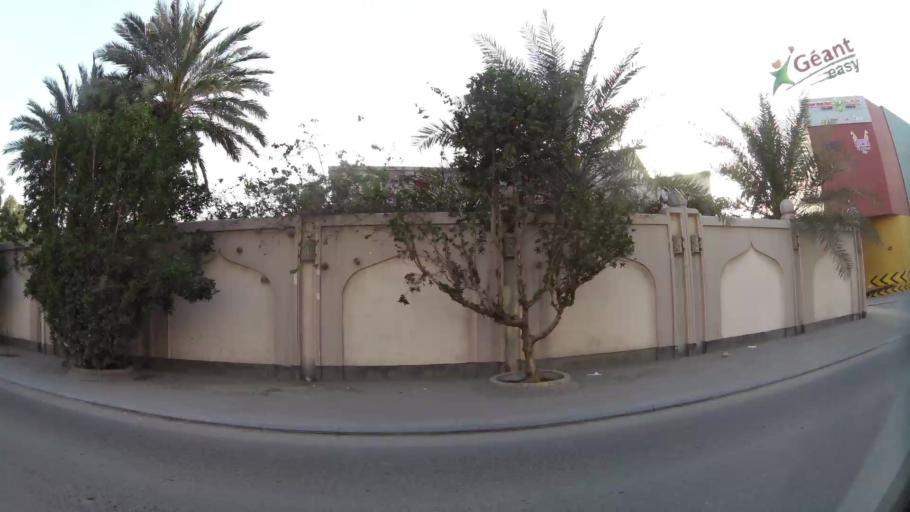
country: BH
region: Manama
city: Jidd Hafs
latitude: 26.2000
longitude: 50.4990
